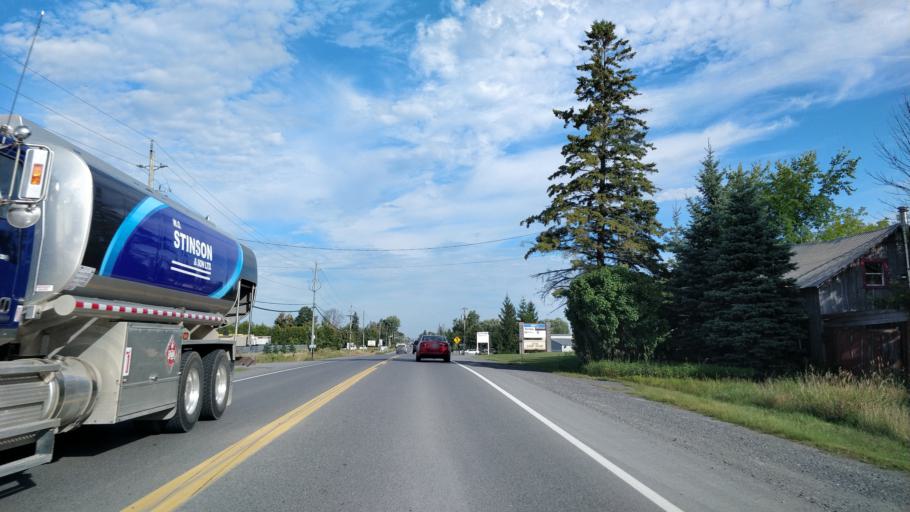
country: CA
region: Ontario
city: Bells Corners
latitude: 45.3011
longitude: -75.9818
